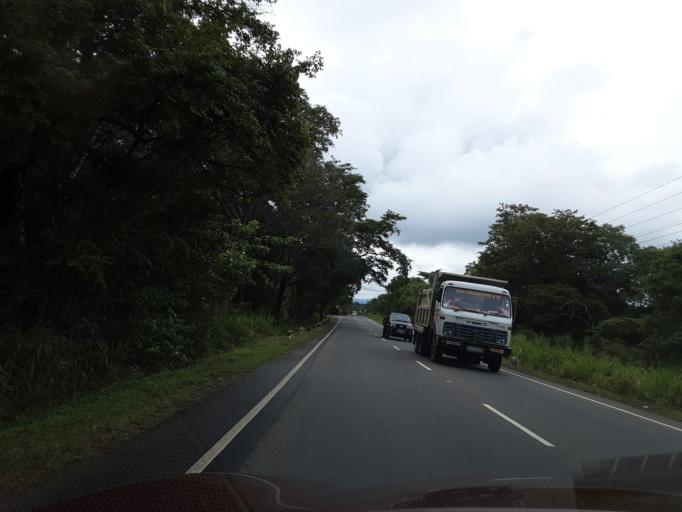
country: LK
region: Uva
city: Badulla
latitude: 7.3982
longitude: 81.1101
